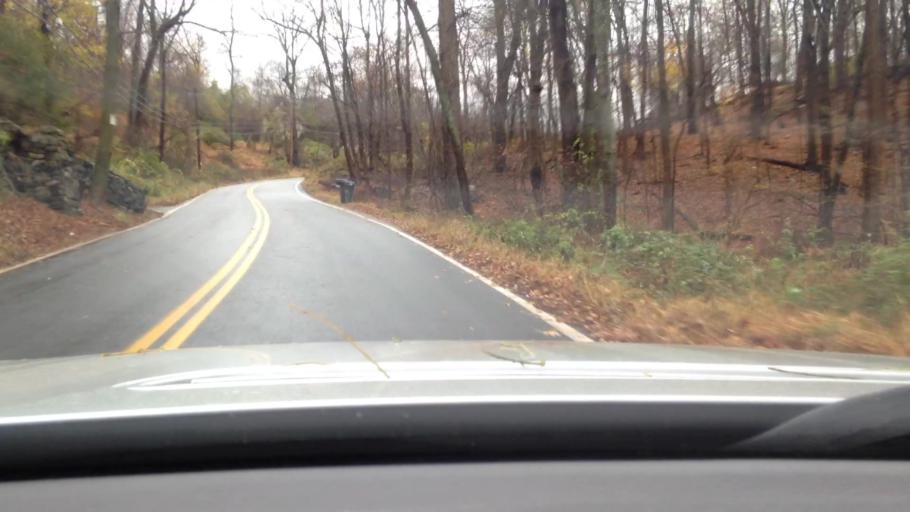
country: US
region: New York
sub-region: Westchester County
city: Croton-on-Hudson
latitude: 41.2305
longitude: -73.8825
